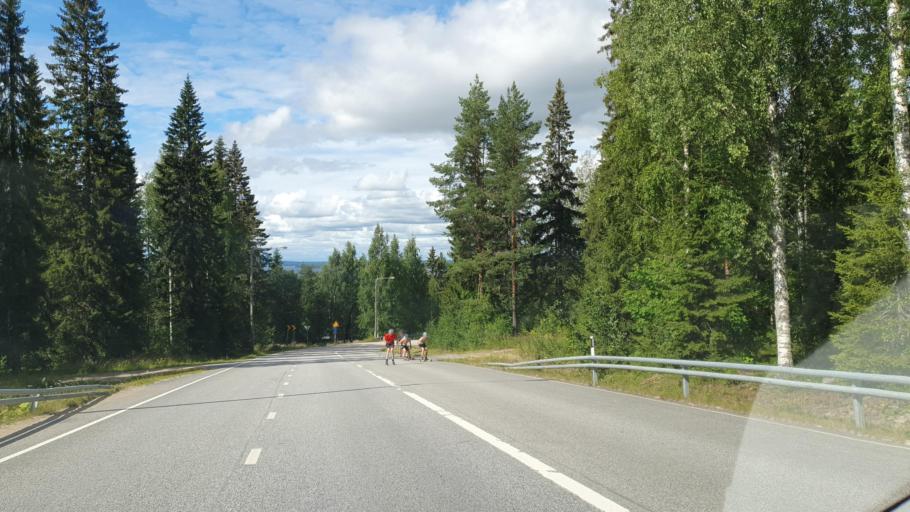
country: FI
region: Kainuu
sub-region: Kajaani
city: Vuokatti
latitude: 64.1302
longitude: 28.2413
